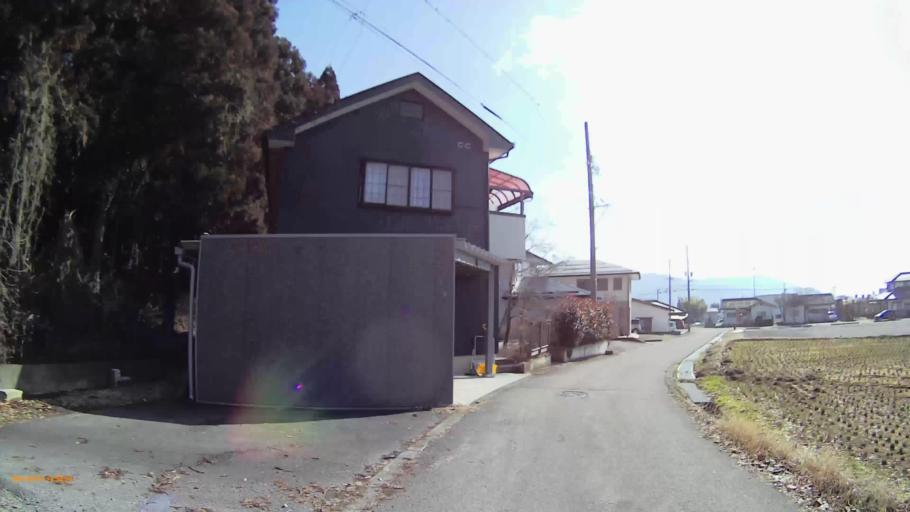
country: JP
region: Nagano
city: Nakano
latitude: 36.7484
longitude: 138.3795
